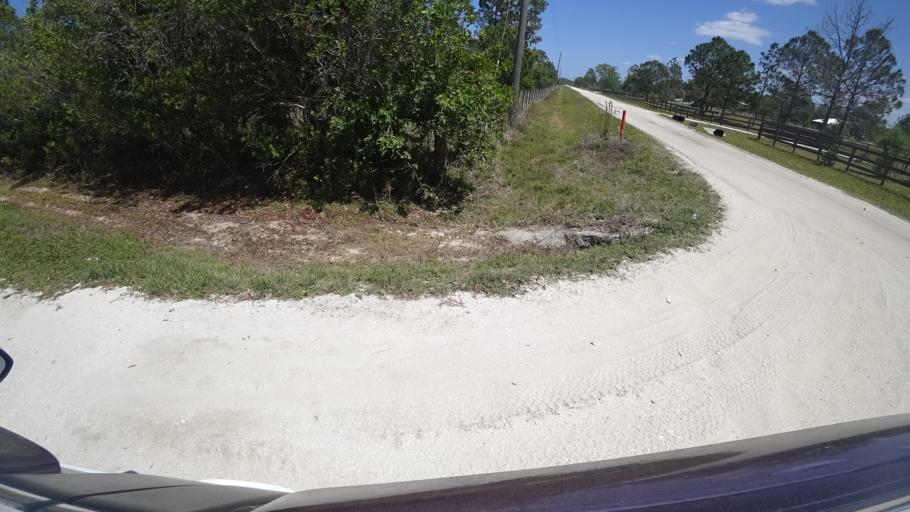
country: US
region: Florida
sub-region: Sarasota County
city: The Meadows
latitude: 27.4257
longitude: -82.3160
